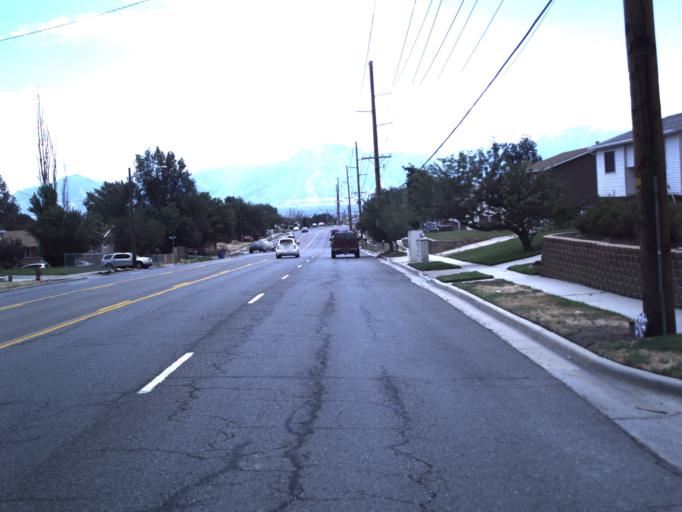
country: US
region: Utah
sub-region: Salt Lake County
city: Kearns
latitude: 40.6530
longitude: -112.0122
